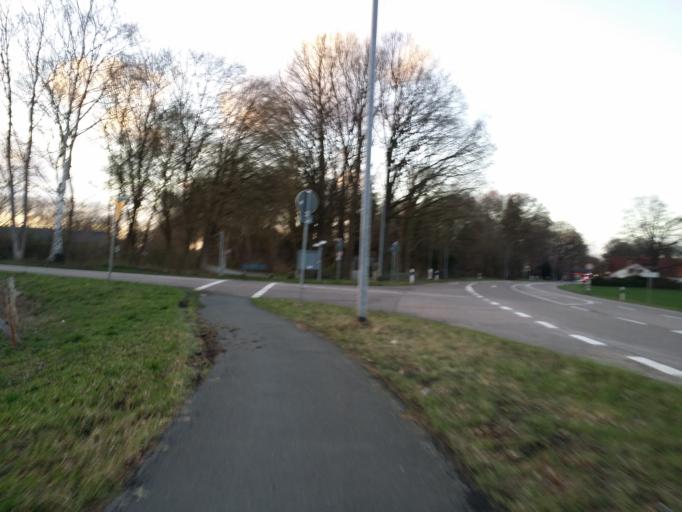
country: DE
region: Lower Saxony
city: Gross Ippener
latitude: 53.0063
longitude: 8.6089
